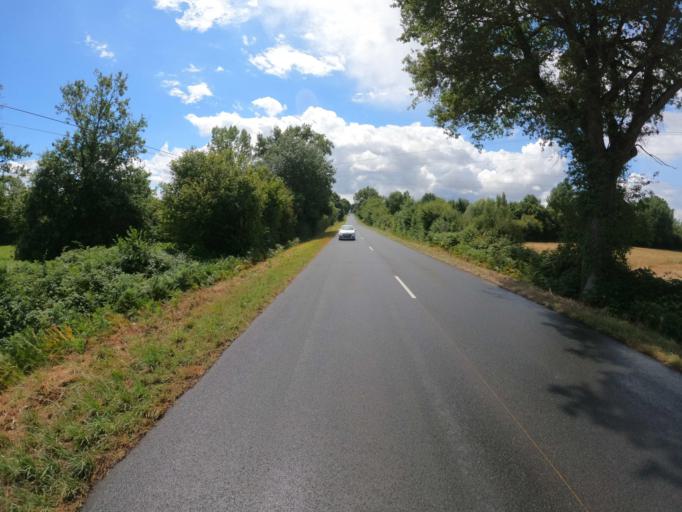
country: FR
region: Pays de la Loire
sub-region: Departement de Maine-et-Loire
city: Feneu
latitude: 47.5985
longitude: -0.5880
